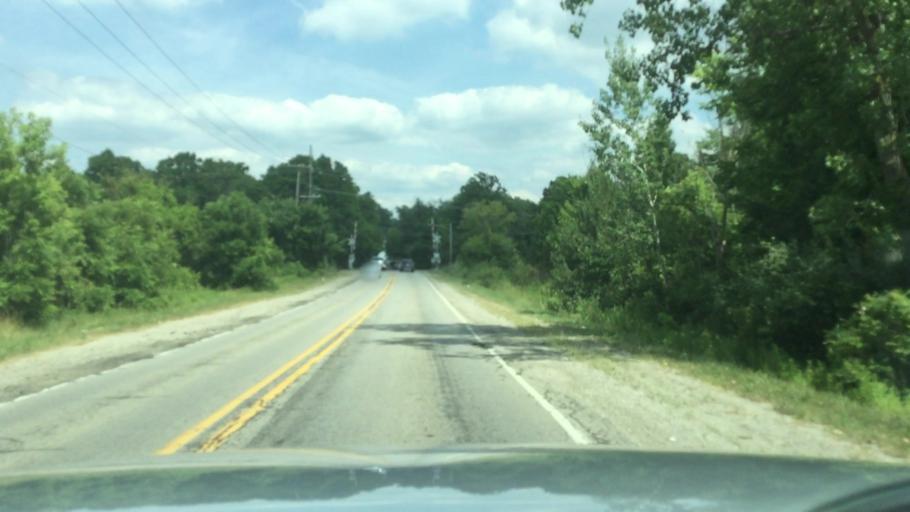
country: US
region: Michigan
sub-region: Genesee County
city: Grand Blanc
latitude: 42.9447
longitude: -83.6436
